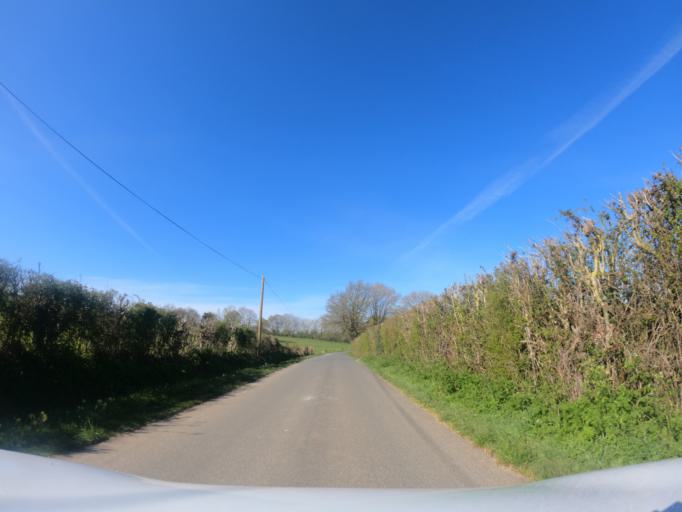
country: FR
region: Pays de la Loire
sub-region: Departement de la Vendee
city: La Tardiere
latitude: 46.6912
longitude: -0.7333
